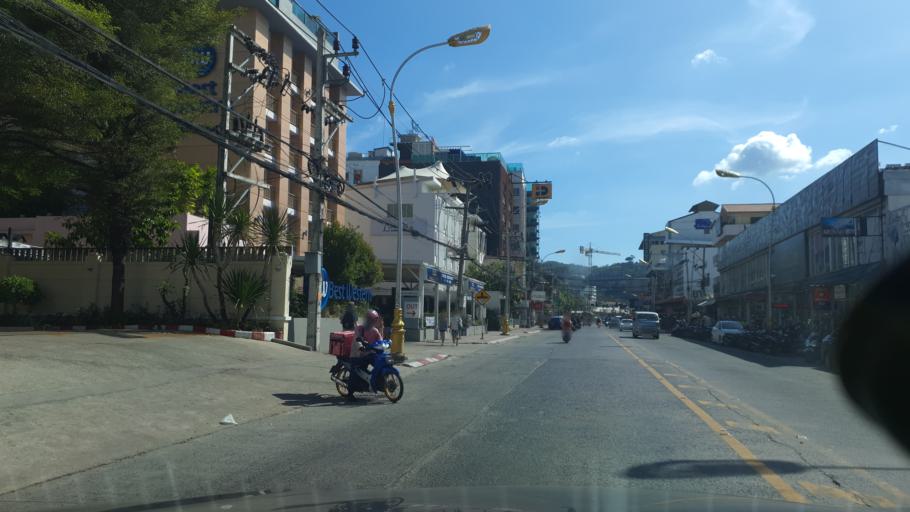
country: TH
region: Phuket
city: Patong
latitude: 7.8932
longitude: 98.3017
